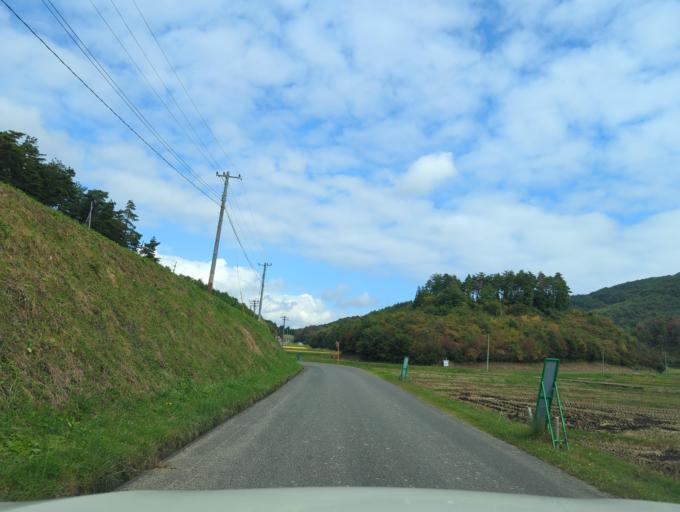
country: JP
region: Fukushima
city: Motomiya
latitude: 37.5181
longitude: 140.3309
